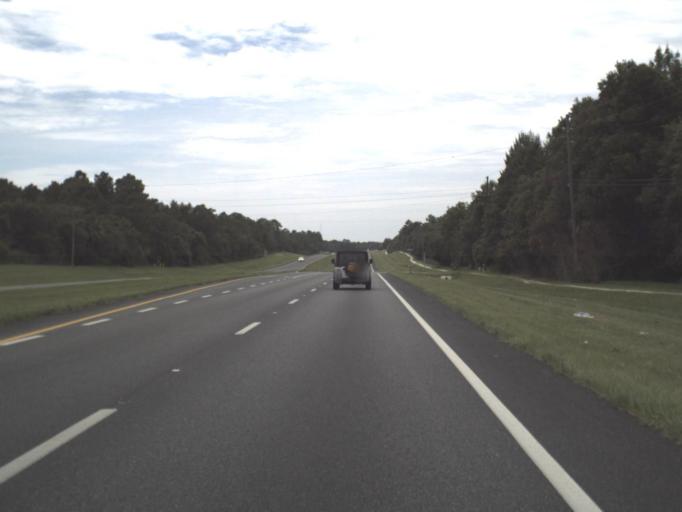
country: US
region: Florida
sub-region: Citrus County
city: Citrus Hills
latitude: 28.8556
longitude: -82.4414
